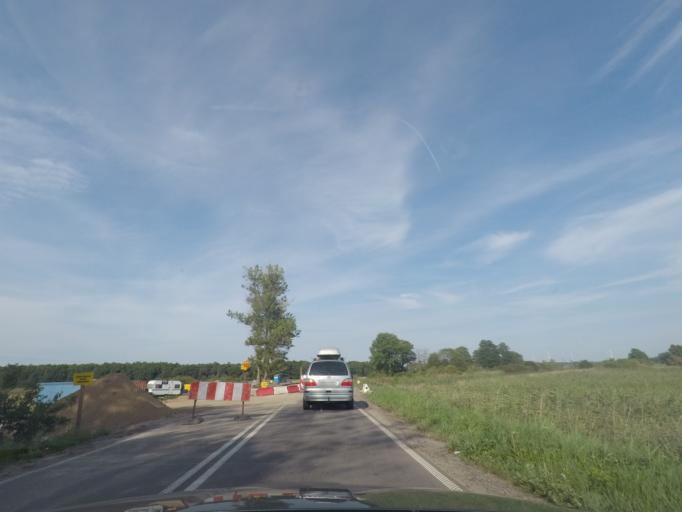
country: PL
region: Pomeranian Voivodeship
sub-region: Powiat leborski
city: Leba
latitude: 54.6541
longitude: 17.5639
